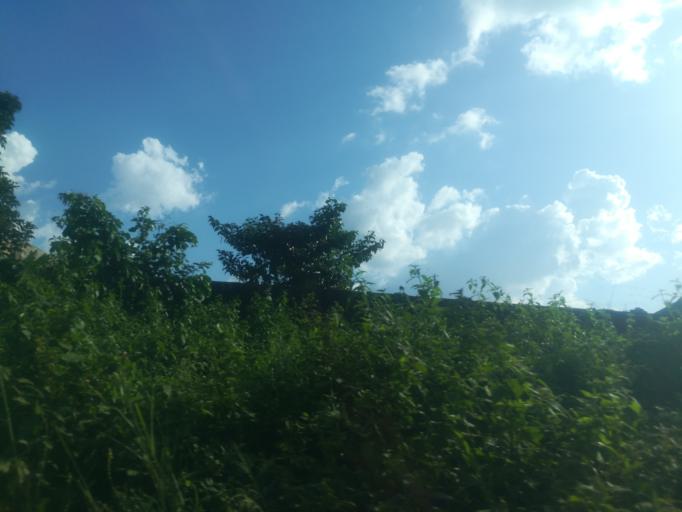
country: NG
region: Oyo
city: Ibadan
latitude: 7.4387
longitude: 3.9639
